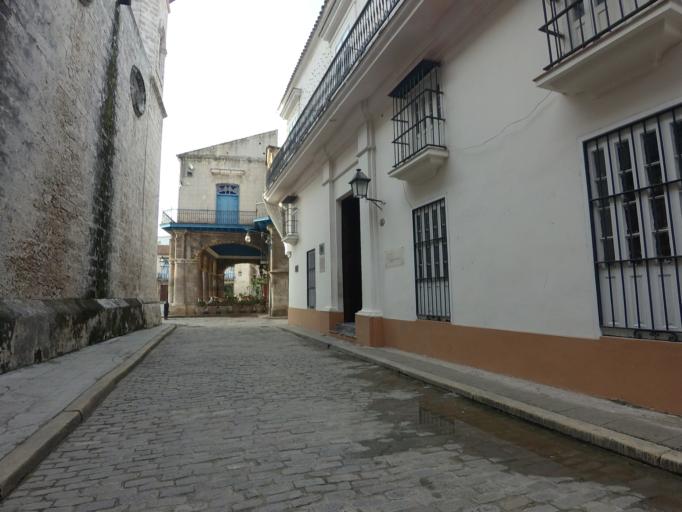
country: CU
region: La Habana
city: La Habana Vieja
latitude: 23.1413
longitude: -82.3519
